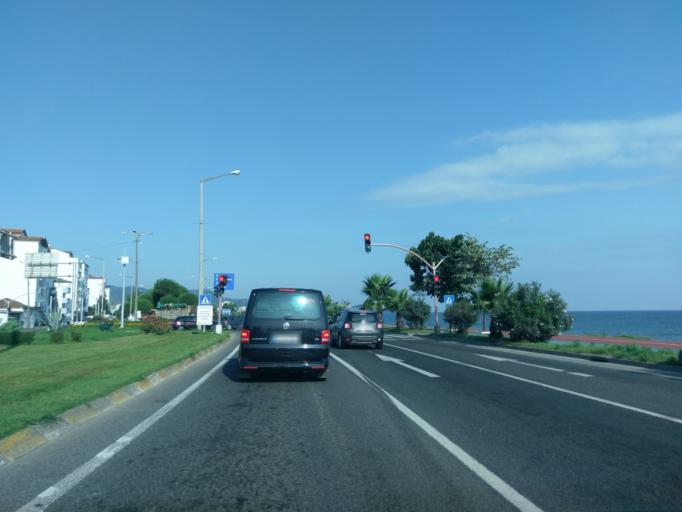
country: TR
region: Ordu
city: Fatsa
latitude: 41.0247
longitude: 37.5235
